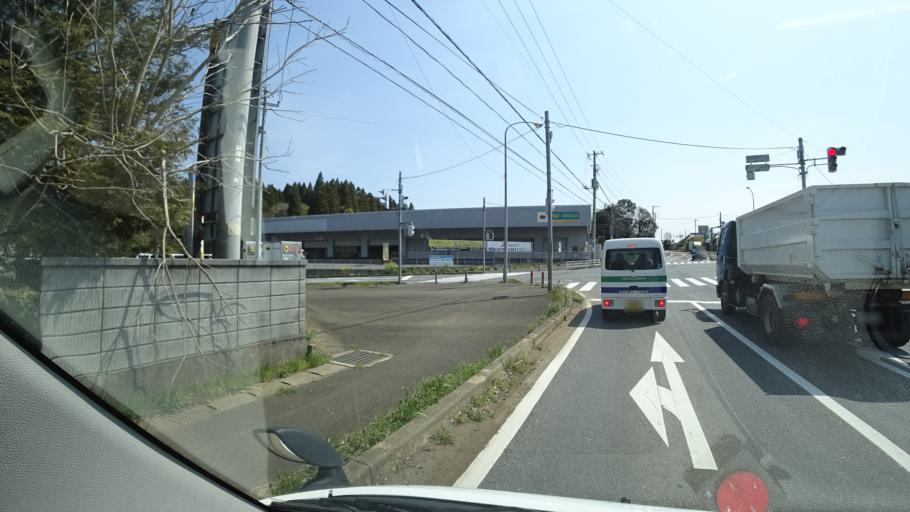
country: JP
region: Chiba
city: Narita
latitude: 35.7201
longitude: 140.3970
